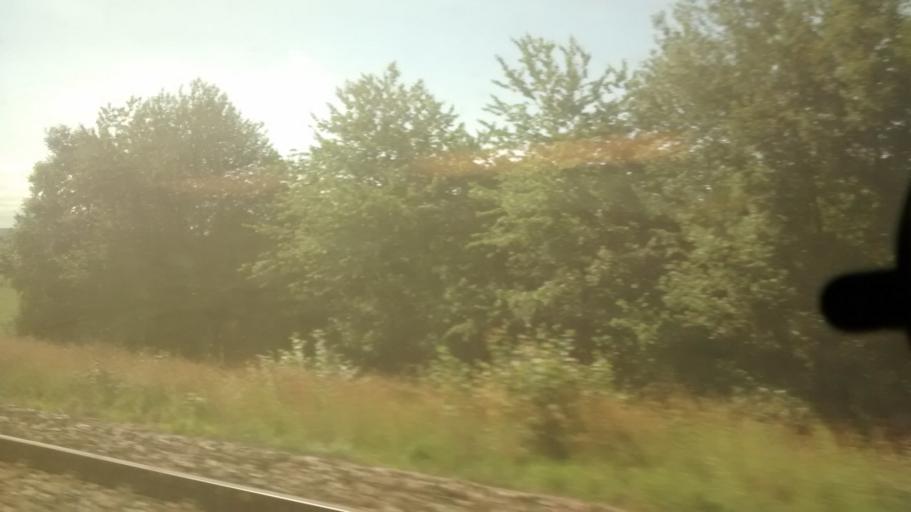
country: FR
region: Pays de la Loire
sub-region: Departement de la Sarthe
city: Thorigne-sur-Due
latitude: 48.0457
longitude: 0.5187
